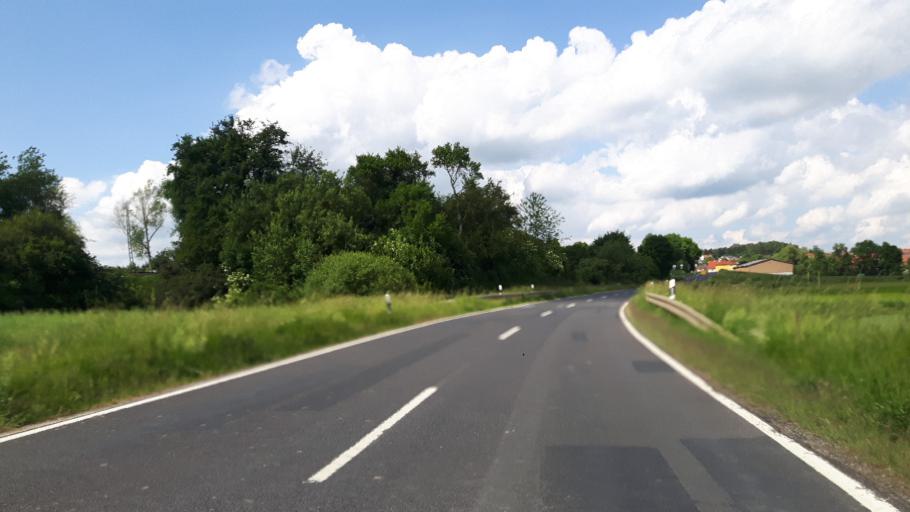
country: DE
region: Bavaria
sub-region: Regierungsbezirk Unterfranken
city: Kirchheim
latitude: 49.6491
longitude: 9.8534
